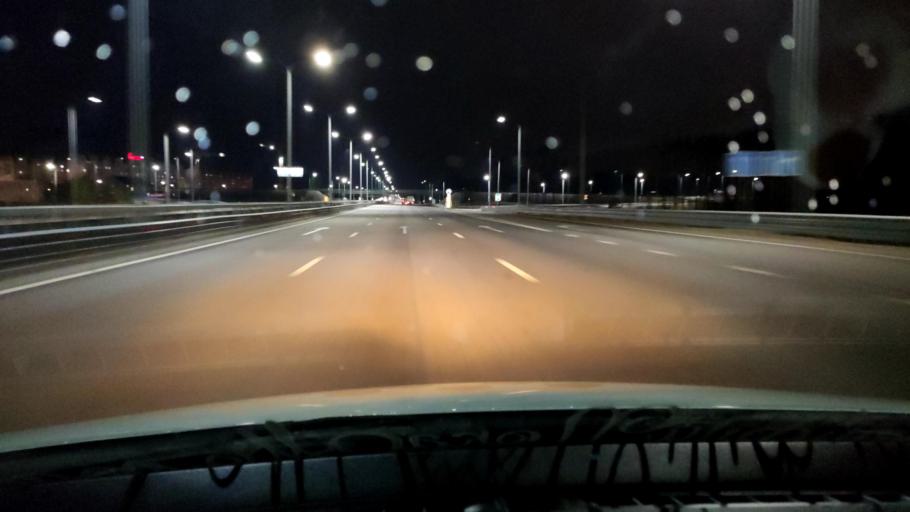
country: RU
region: Voronezj
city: Somovo
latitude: 51.7455
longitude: 39.3061
